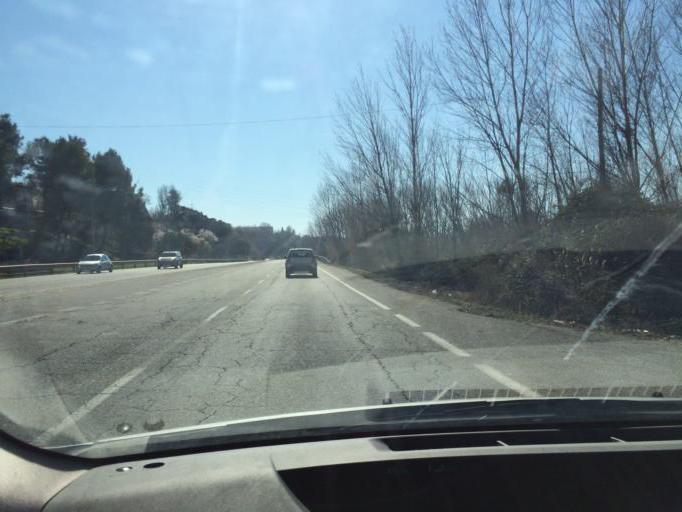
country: ES
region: Catalonia
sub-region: Provincia de Barcelona
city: Sant Joan de Vilatorrada
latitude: 41.7372
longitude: 1.8103
